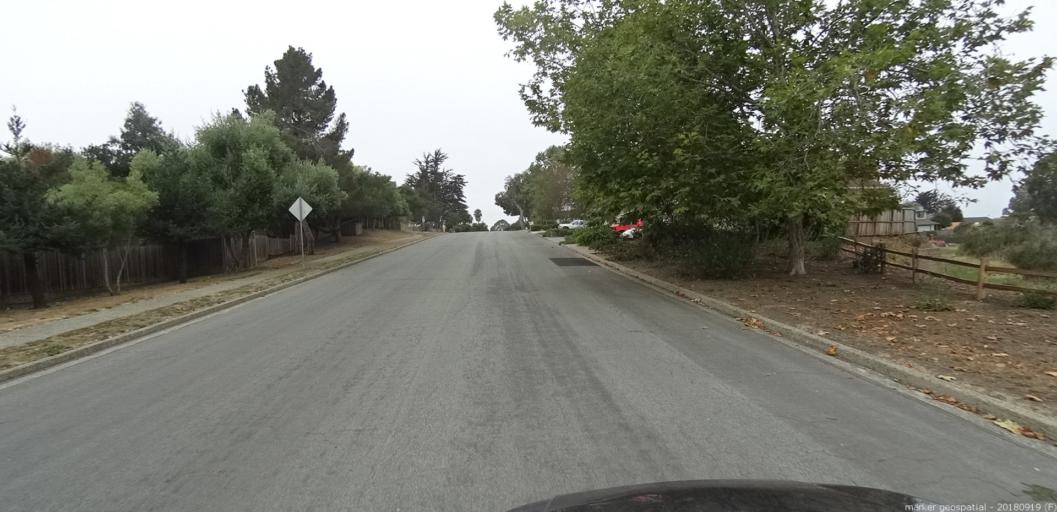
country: US
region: California
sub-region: Monterey County
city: Castroville
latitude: 36.7749
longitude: -121.7263
